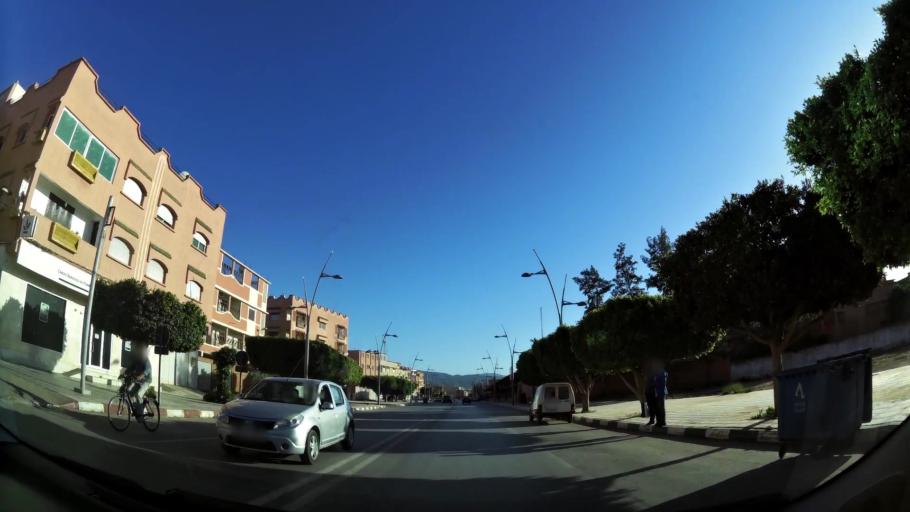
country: MA
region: Oriental
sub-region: Berkane-Taourirt
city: Berkane
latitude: 34.9331
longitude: -2.3257
